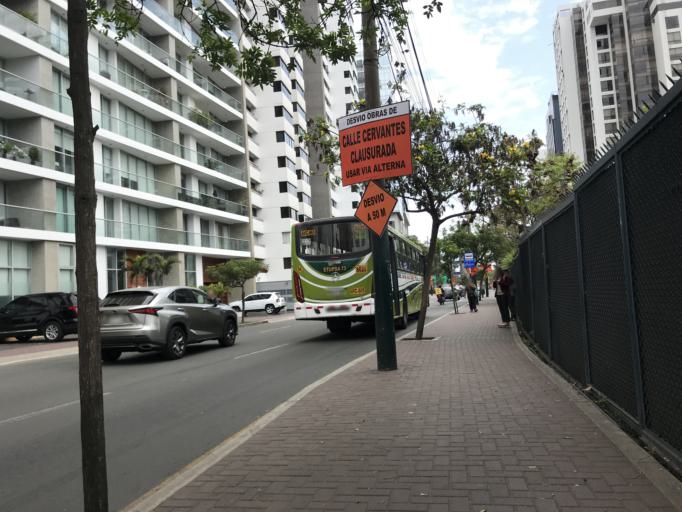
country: PE
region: Lima
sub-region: Lima
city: San Isidro
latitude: -12.1028
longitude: -77.0385
